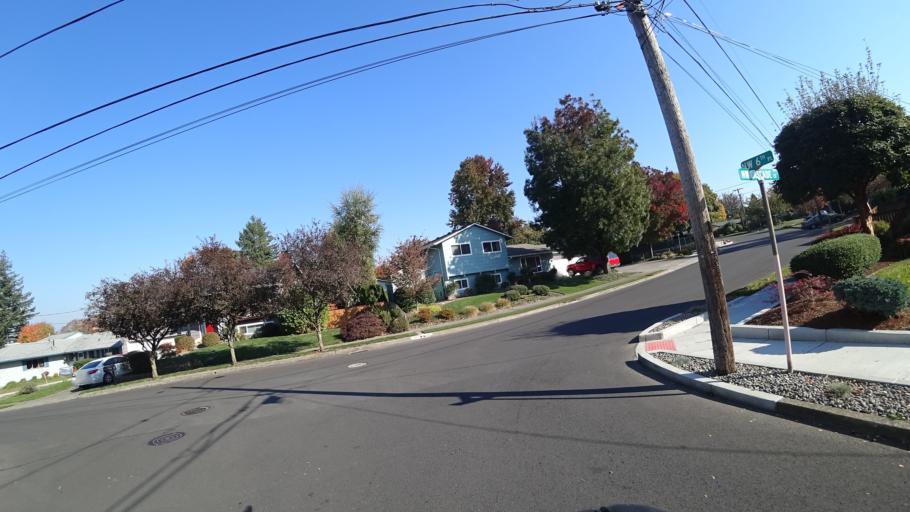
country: US
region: Oregon
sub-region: Multnomah County
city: Gresham
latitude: 45.5020
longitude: -122.4544
